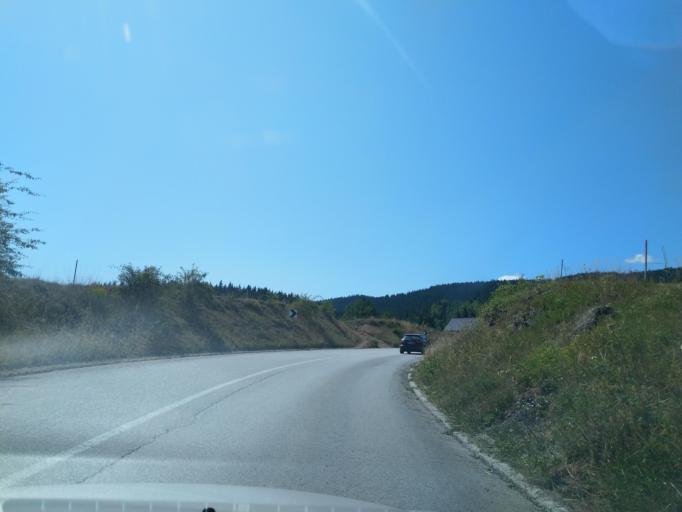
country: RS
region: Central Serbia
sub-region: Zlatiborski Okrug
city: Nova Varos
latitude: 43.4212
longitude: 19.8290
